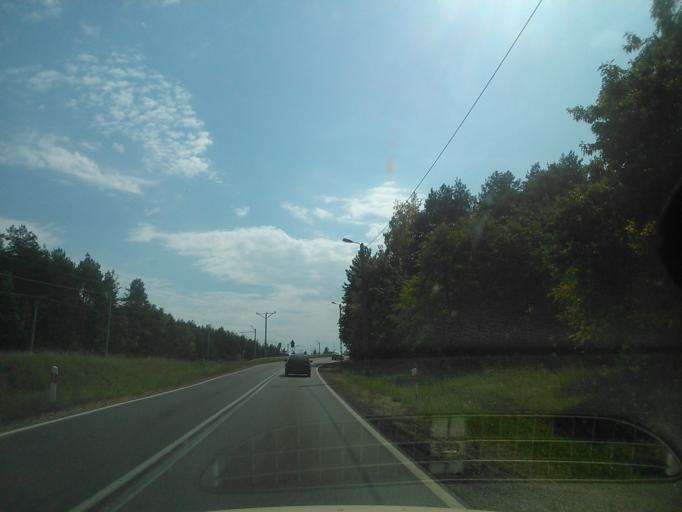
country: PL
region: Warmian-Masurian Voivodeship
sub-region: Powiat dzialdowski
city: Ilowo -Osada
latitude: 53.1456
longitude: 20.3389
